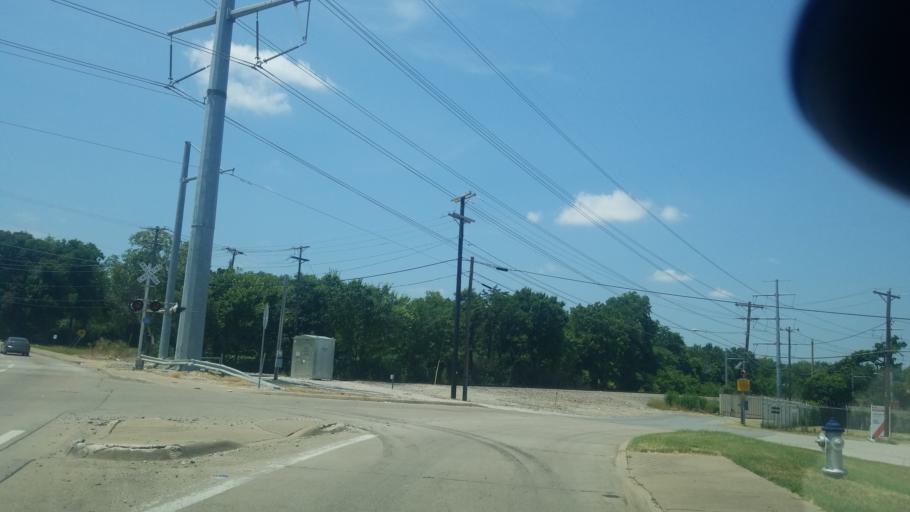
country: US
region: Texas
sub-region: Dallas County
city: Dallas
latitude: 32.7235
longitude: -96.7682
